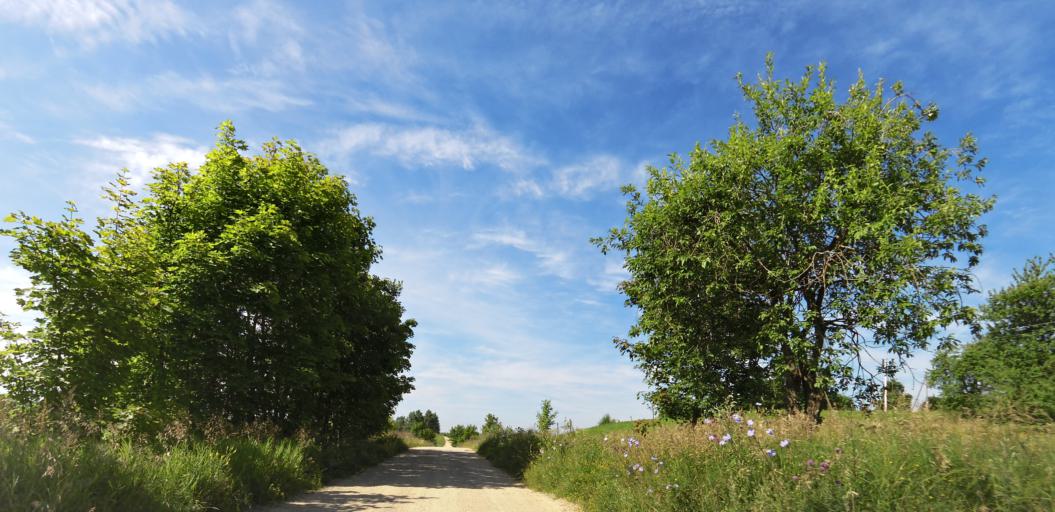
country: LT
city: Grigiskes
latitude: 54.7797
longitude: 25.0689
